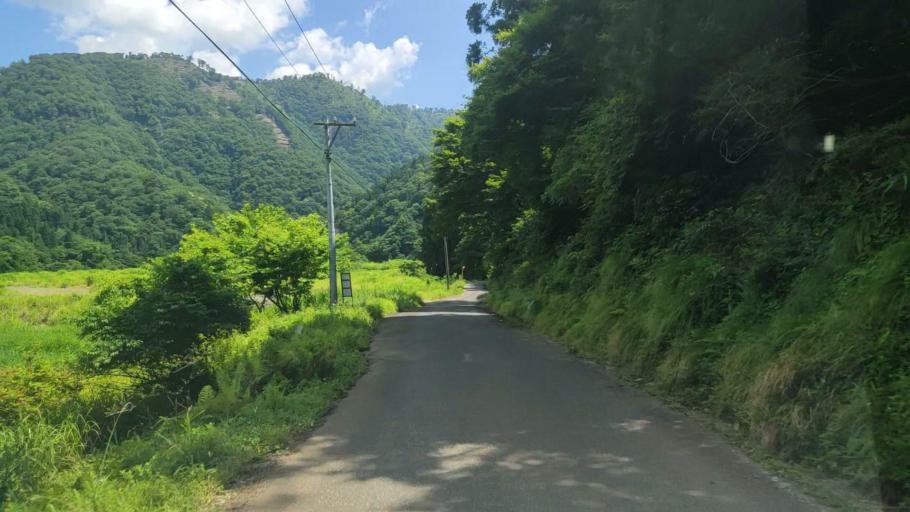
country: JP
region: Fukui
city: Ono
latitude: 35.7493
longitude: 136.5800
